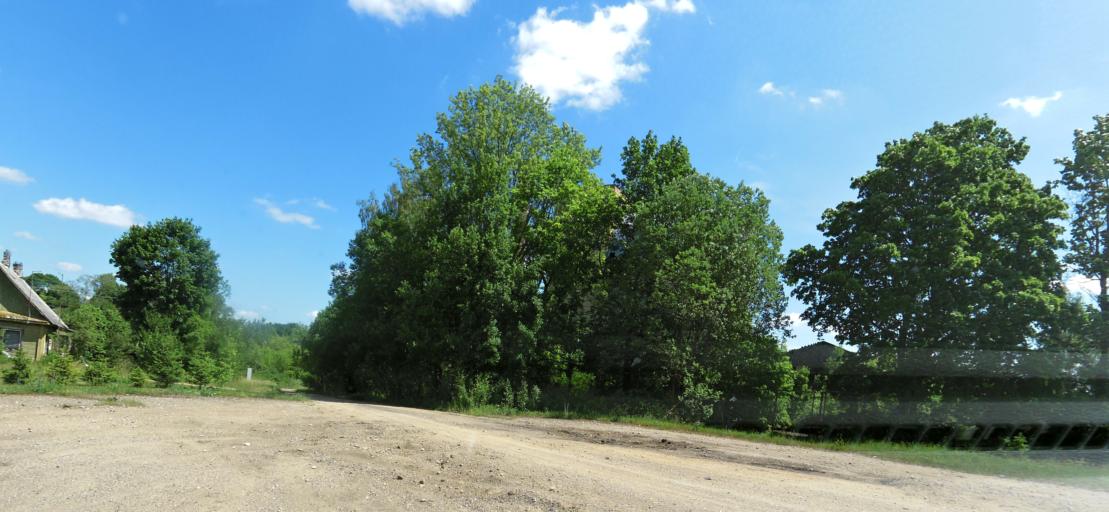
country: LT
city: Nemencine
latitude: 54.8716
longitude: 25.5380
